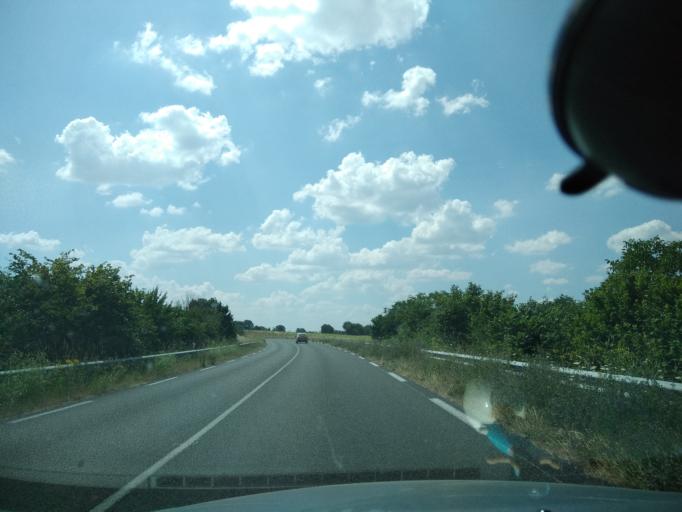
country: FR
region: Centre
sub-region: Departement d'Indre-et-Loire
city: Blere
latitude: 47.3173
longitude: 1.0072
